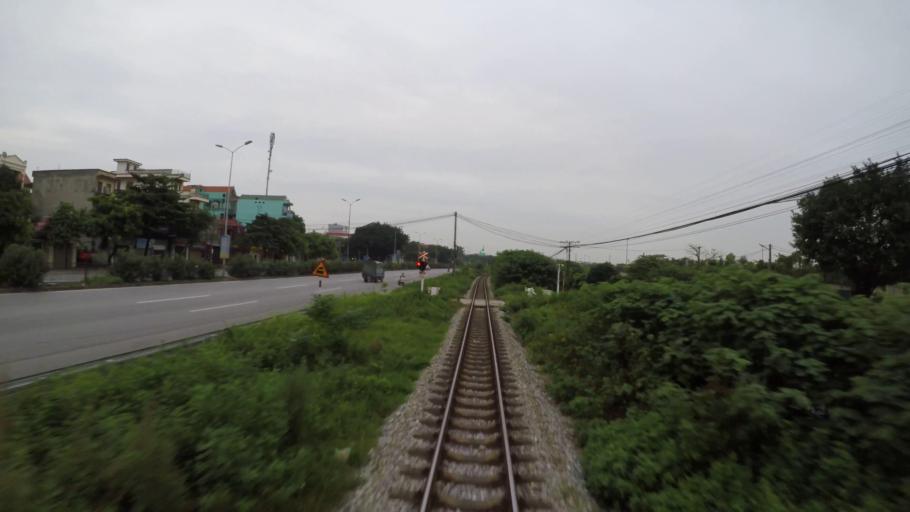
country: VN
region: Ha Noi
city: Trau Quy
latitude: 21.0114
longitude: 105.9515
